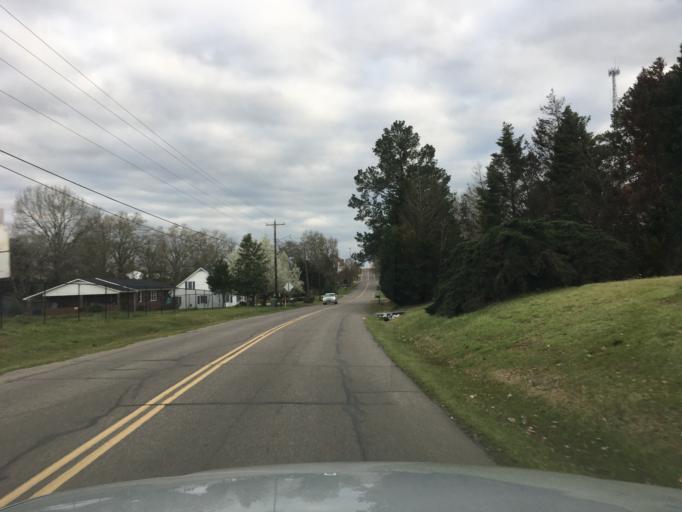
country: US
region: South Carolina
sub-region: Saluda County
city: Saluda
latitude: 34.0062
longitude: -81.7740
